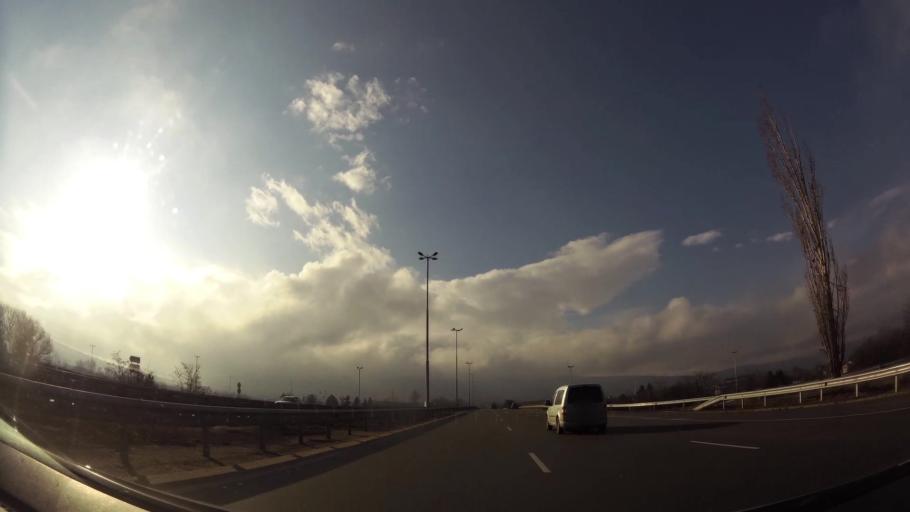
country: BG
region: Sofia-Capital
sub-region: Stolichna Obshtina
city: Sofia
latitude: 42.6343
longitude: 23.4483
